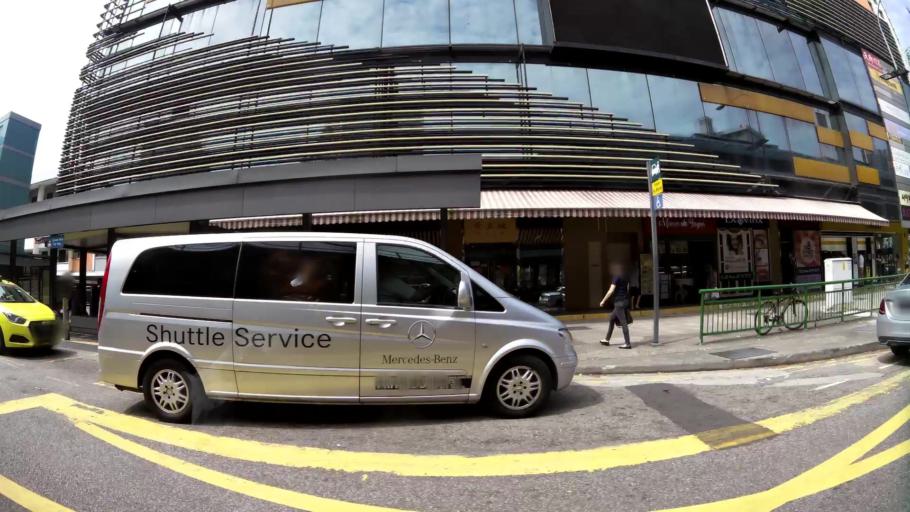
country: SG
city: Singapore
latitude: 1.3144
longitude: 103.7652
